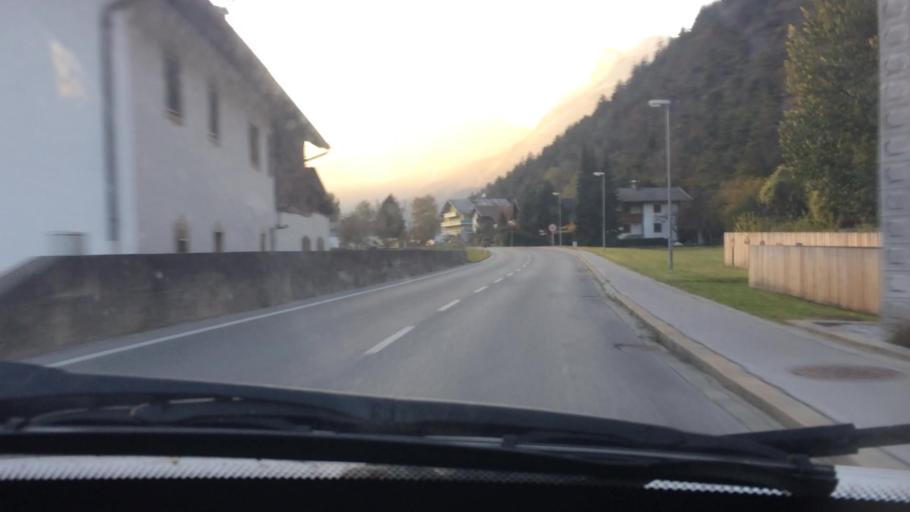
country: AT
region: Tyrol
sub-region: Politischer Bezirk Innsbruck Land
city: Hatting
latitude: 47.2922
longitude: 11.1596
